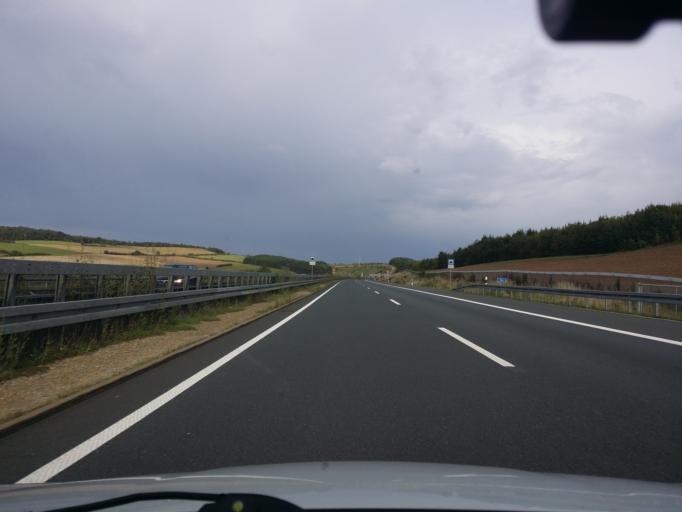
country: DE
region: Thuringia
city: Arenshausen
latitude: 51.3967
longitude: 9.9609
